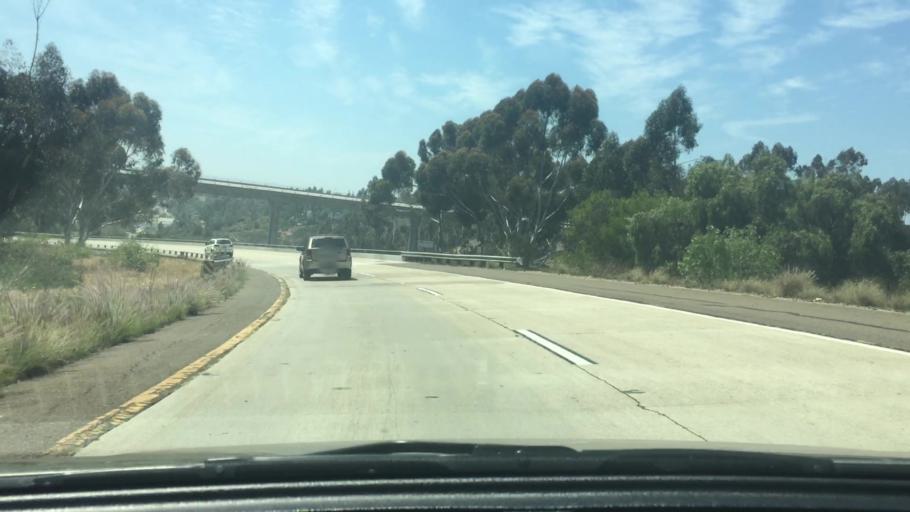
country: US
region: California
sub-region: San Diego County
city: National City
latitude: 32.7201
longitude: -117.1016
